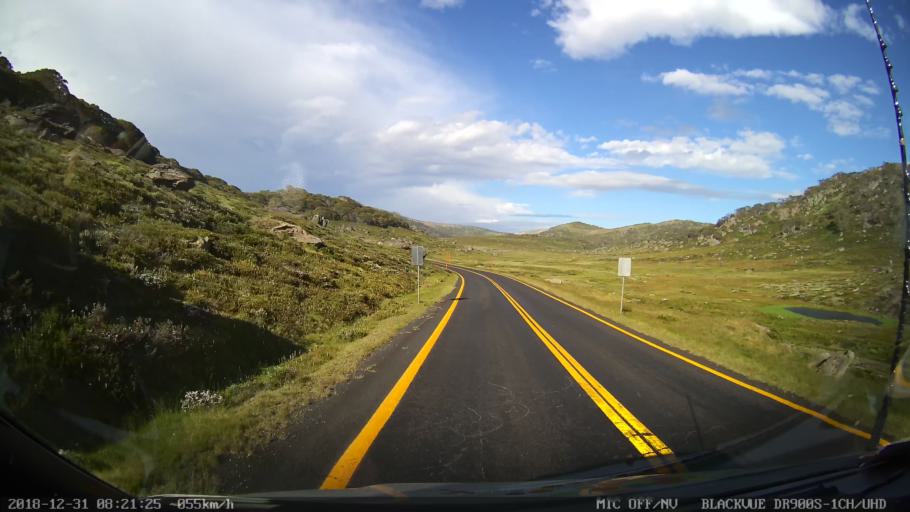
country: AU
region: New South Wales
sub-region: Snowy River
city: Jindabyne
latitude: -36.4274
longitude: 148.3678
